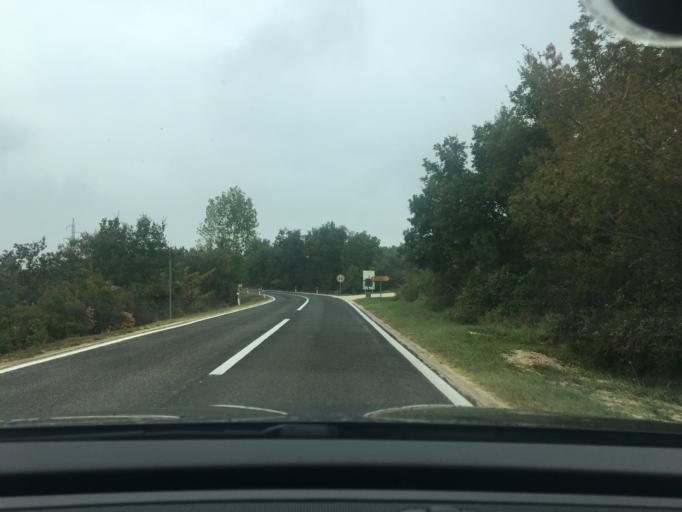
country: HR
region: Istarska
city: Buje
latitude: 45.4263
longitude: 13.6588
